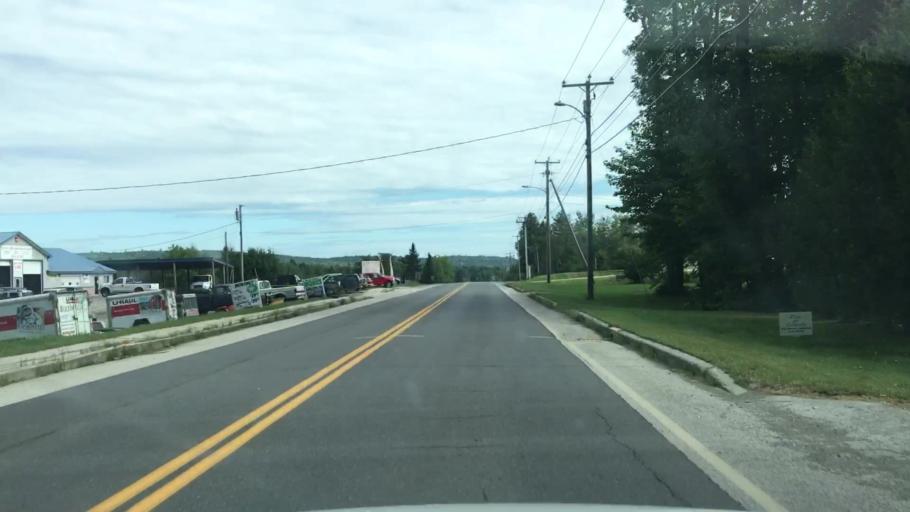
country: US
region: Maine
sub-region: Piscataquis County
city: Dover-Foxcroft
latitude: 45.1932
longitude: -69.2183
